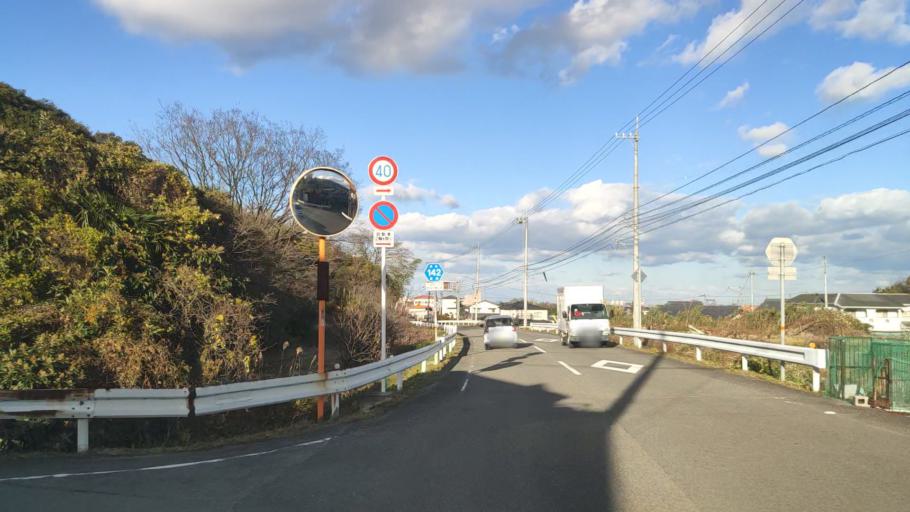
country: JP
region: Ehime
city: Saijo
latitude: 33.8896
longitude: 133.1308
